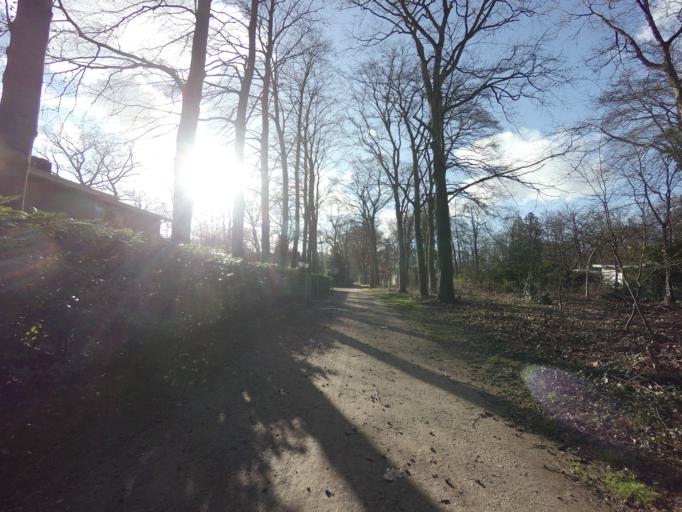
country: NL
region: North Holland
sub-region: Gemeente Hilversum
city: Hilversum
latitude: 52.2400
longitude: 5.1493
